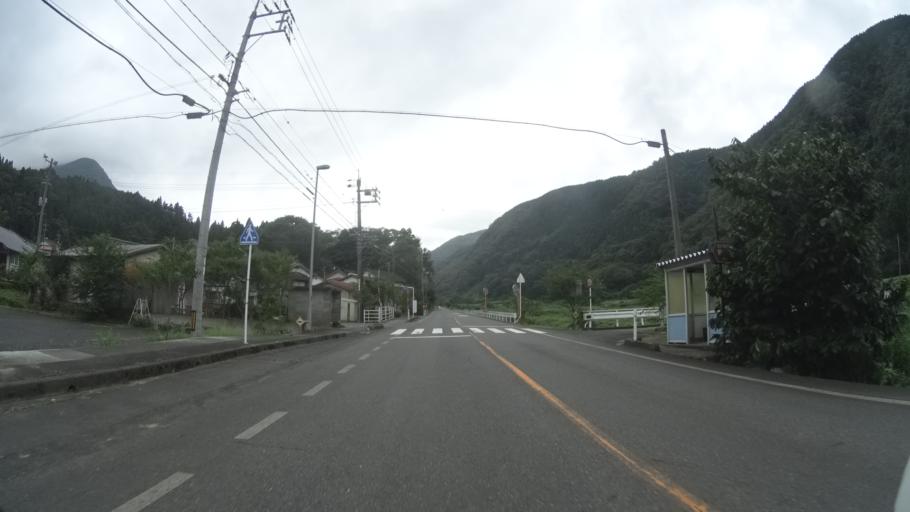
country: JP
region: Tottori
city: Kurayoshi
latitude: 35.4440
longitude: 134.0266
